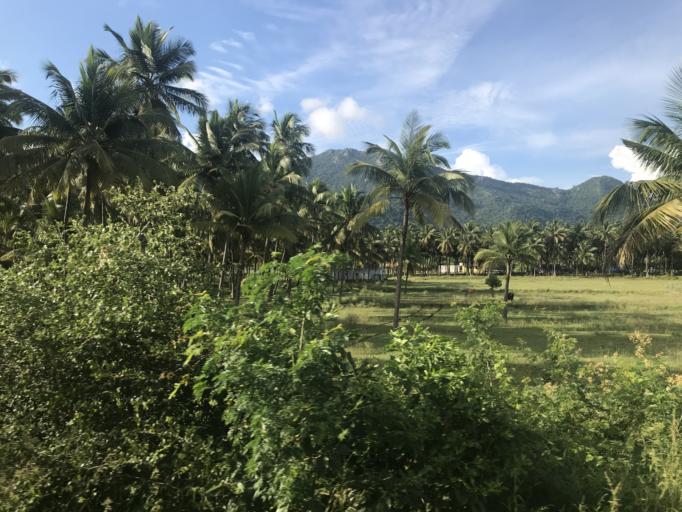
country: IN
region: Tamil Nadu
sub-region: Coimbatore
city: Madukkarai
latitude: 10.8772
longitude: 76.8617
